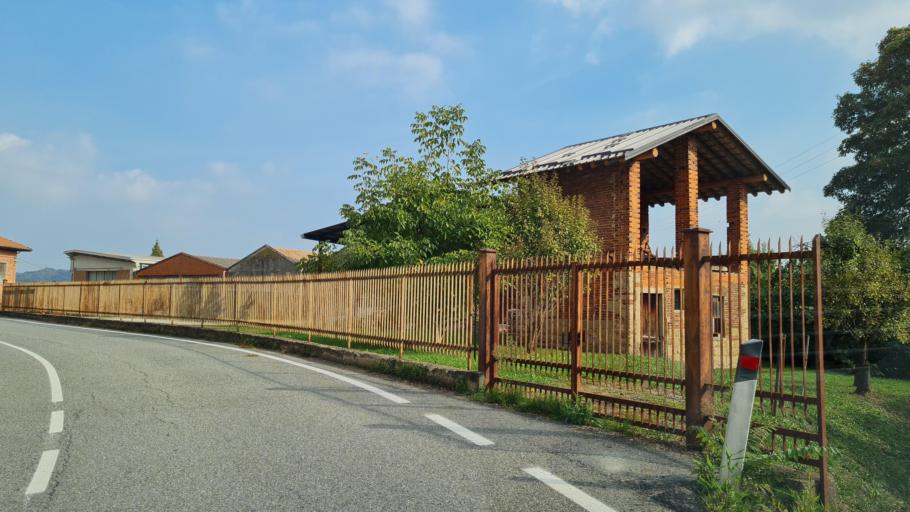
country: IT
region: Piedmont
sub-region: Provincia di Biella
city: Mezzana Mortigliengo
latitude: 45.6240
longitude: 8.1823
